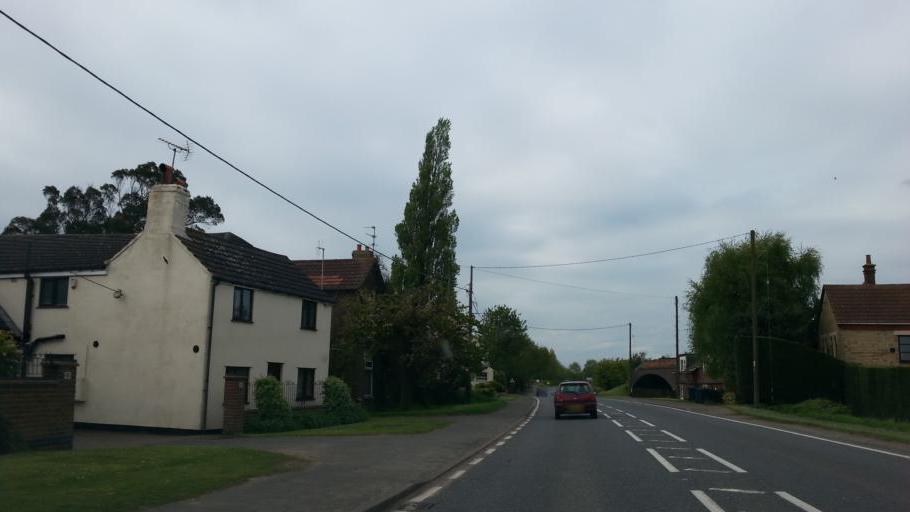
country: GB
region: England
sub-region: Cambridgeshire
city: March
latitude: 52.6023
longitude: 0.0630
